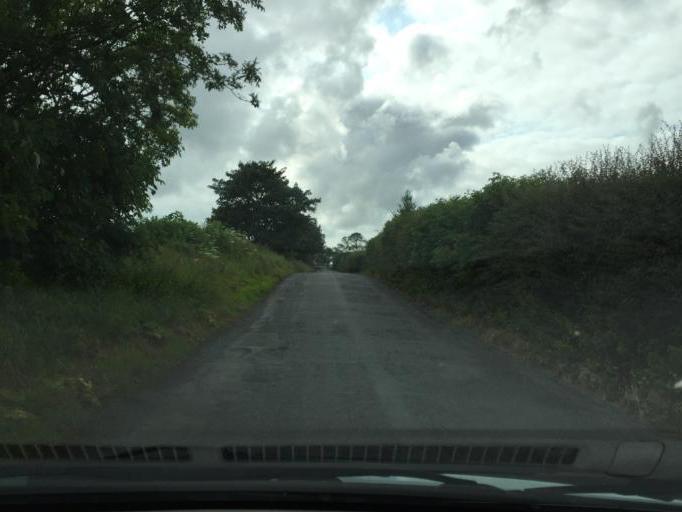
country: IE
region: Connaught
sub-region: Sligo
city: Sligo
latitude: 54.2878
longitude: -8.4778
